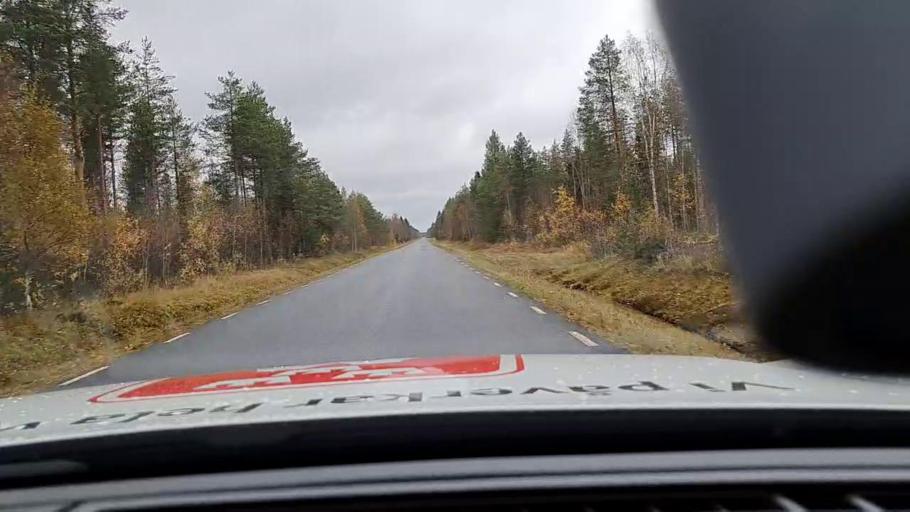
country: SE
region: Norrbotten
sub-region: Haparanda Kommun
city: Haparanda
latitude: 65.9105
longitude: 23.8296
